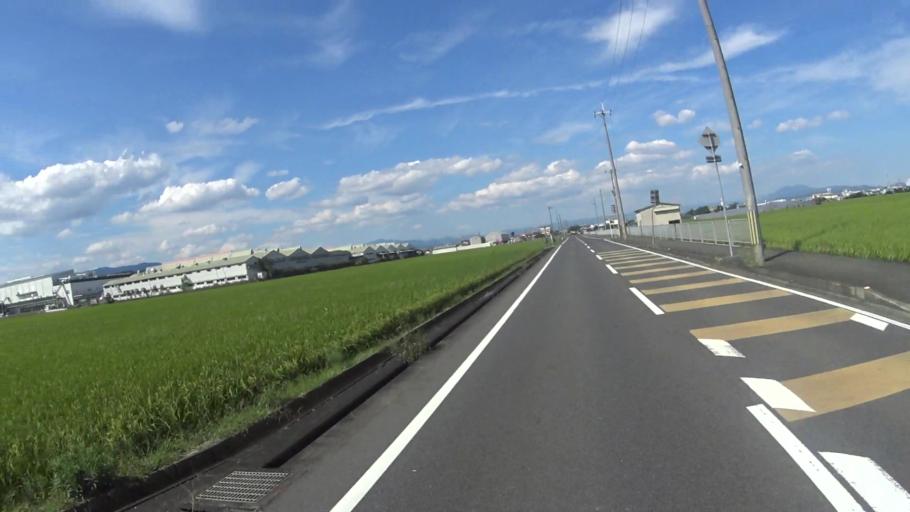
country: JP
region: Kyoto
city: Yawata
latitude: 34.8585
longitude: 135.7215
